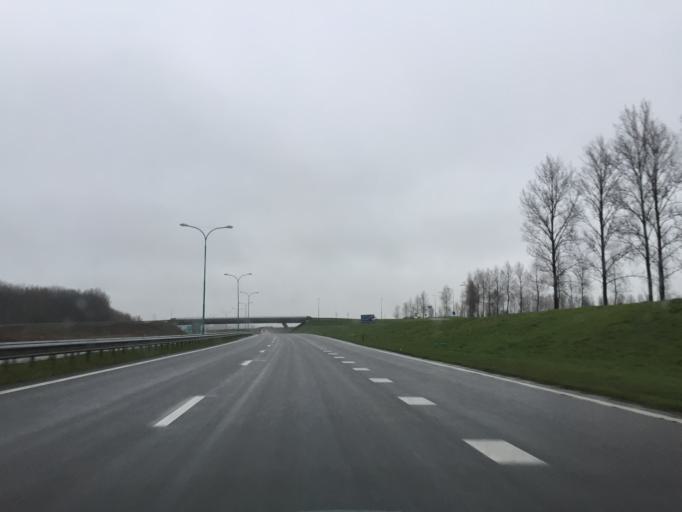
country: NL
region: Zeeland
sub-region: Gemeente Borsele
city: Borssele
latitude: 51.4495
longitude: 3.7509
